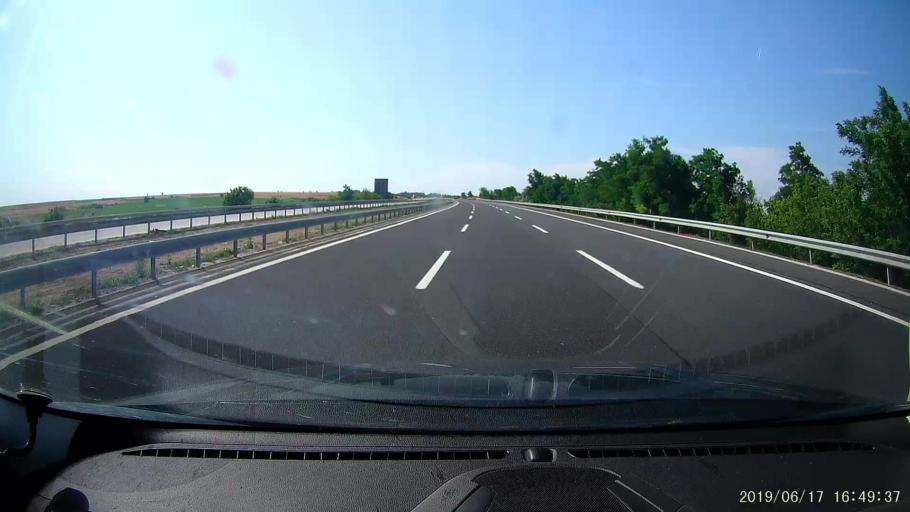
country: TR
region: Kirklareli
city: Babaeski
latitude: 41.5118
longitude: 27.1094
